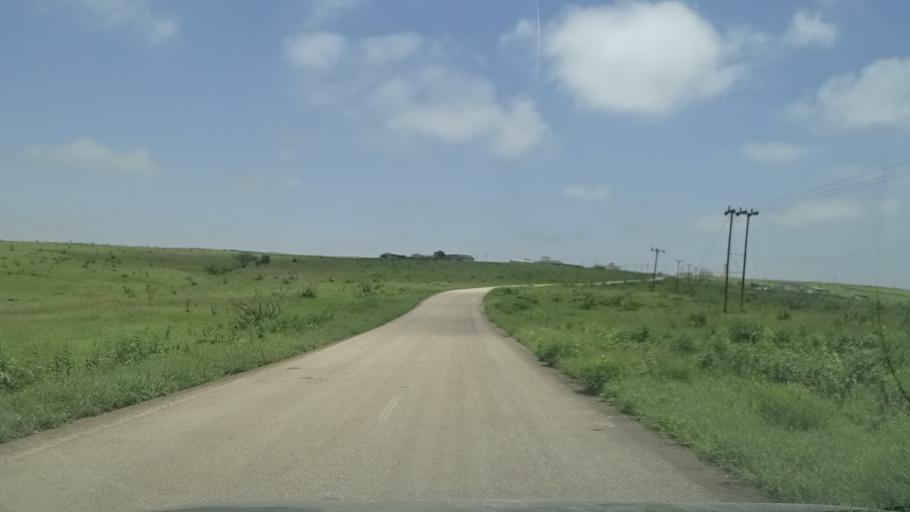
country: OM
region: Zufar
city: Salalah
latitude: 17.2273
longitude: 54.2074
